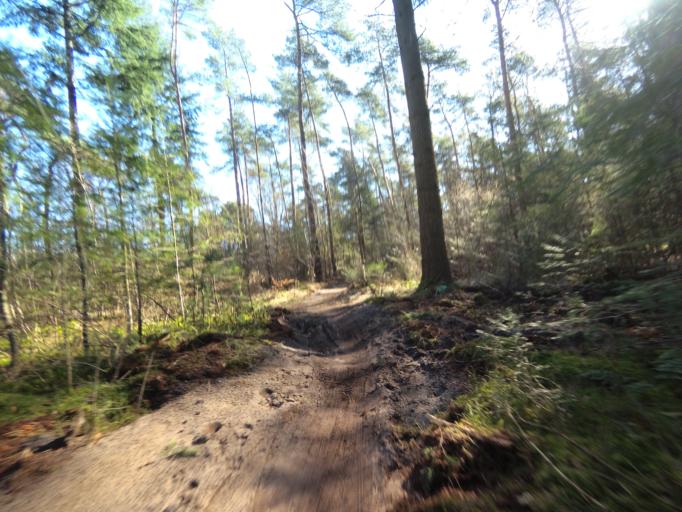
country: NL
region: Utrecht
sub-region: Gemeente Utrechtse Heuvelrug
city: Maarn
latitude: 52.0929
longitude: 5.3397
